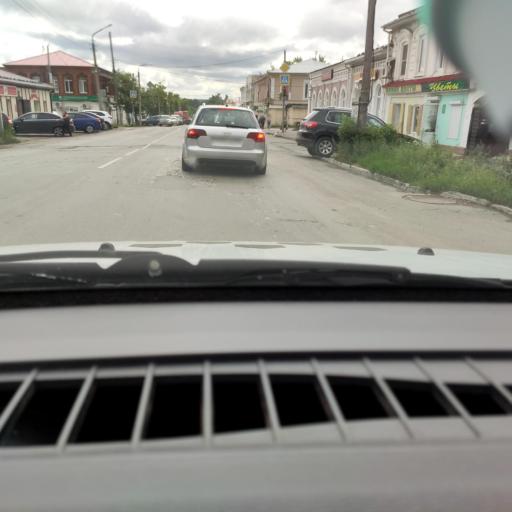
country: RU
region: Sverdlovsk
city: Krasnoufimsk
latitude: 56.6210
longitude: 57.7706
